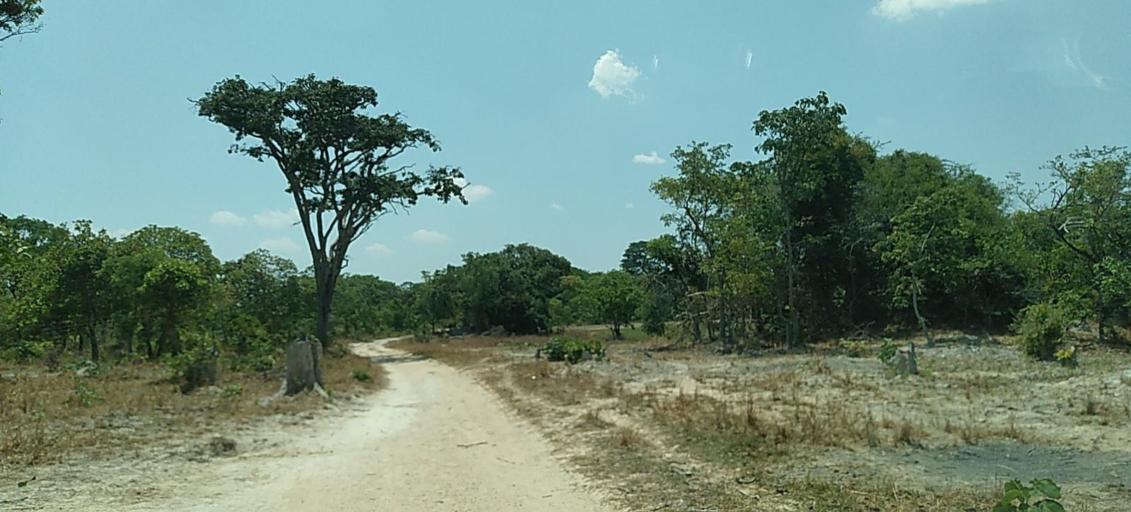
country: ZM
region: Central
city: Kapiri Mposhi
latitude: -13.6707
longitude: 28.4999
